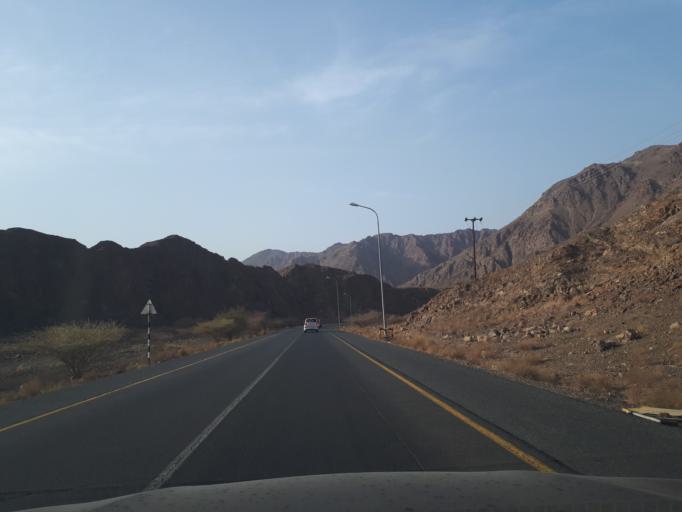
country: OM
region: Muhafazat ad Dakhiliyah
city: Sufalat Sama'il
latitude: 23.1749
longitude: 58.0955
